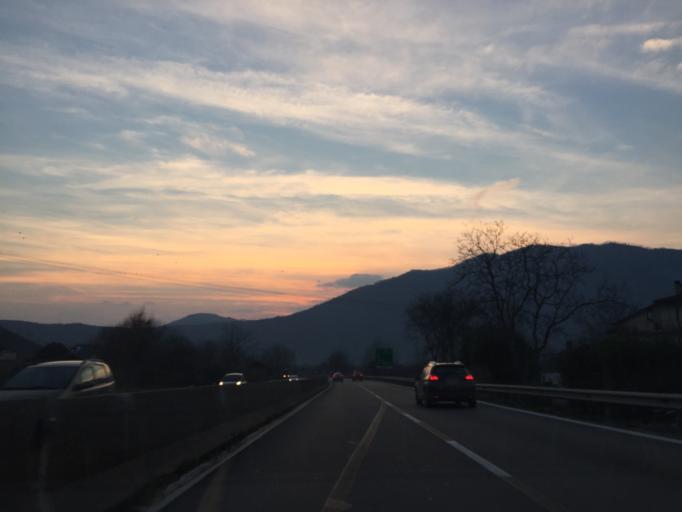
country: IT
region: Campania
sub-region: Provincia di Avellino
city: San Pietro
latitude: 40.8168
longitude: 14.7832
